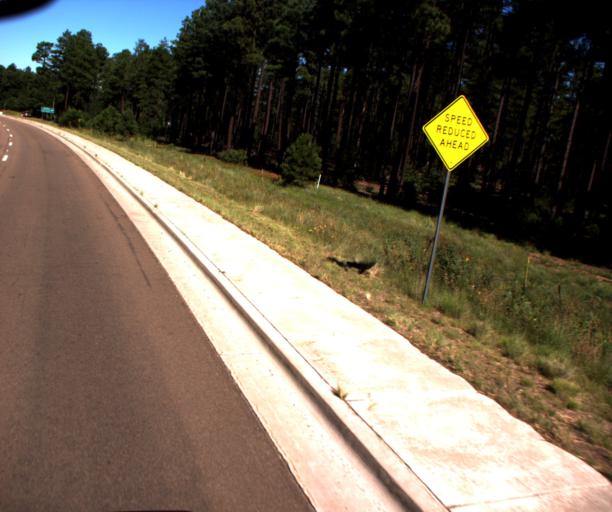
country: US
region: Arizona
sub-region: Navajo County
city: Pinetop-Lakeside
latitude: 34.1221
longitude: -109.9198
